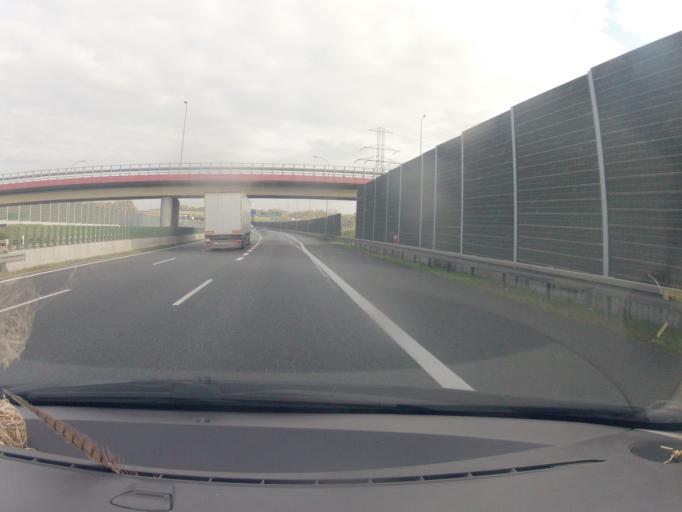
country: PL
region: Lesser Poland Voivodeship
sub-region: Powiat wielicki
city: Czarnochowice
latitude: 50.0069
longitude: 20.0530
